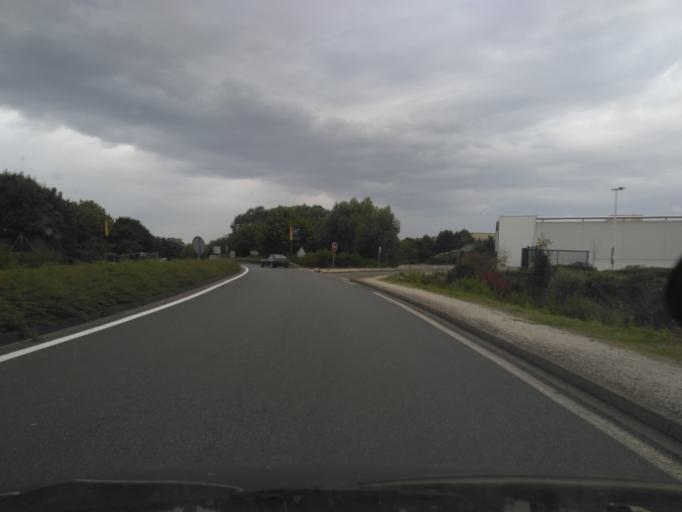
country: FR
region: Ile-de-France
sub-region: Departement de Seine-et-Marne
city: Savigny-le-Temple
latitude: 48.5895
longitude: 2.5997
